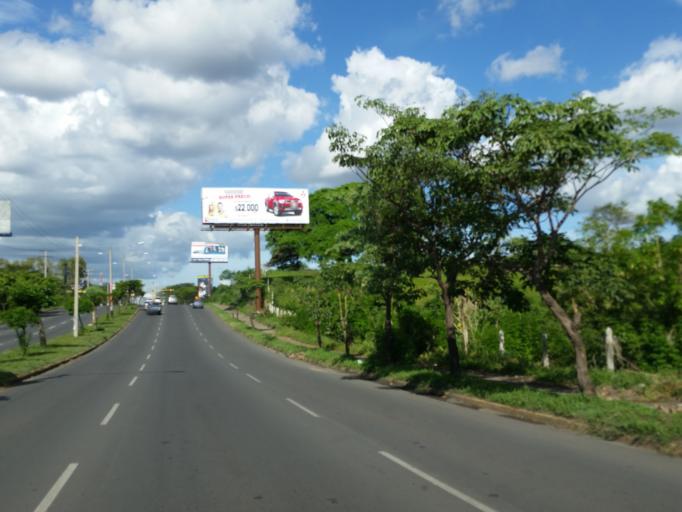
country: NI
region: Managua
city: Managua
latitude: 12.1091
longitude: -86.2813
